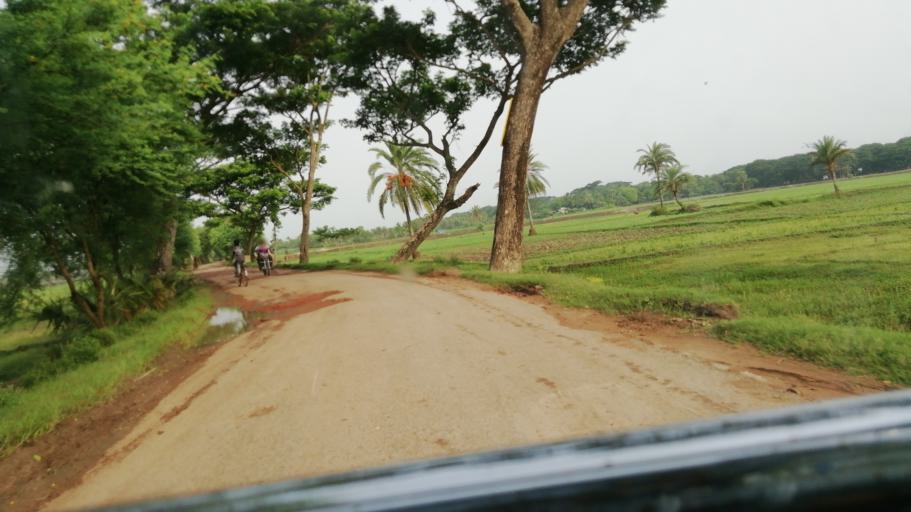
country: BD
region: Khulna
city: Bhatpara Abhaynagar
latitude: 23.0401
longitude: 89.3146
